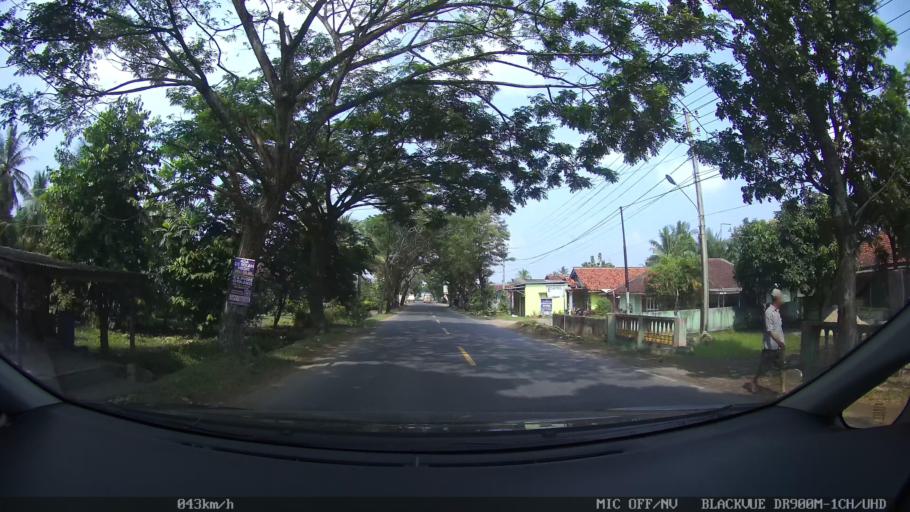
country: ID
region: Lampung
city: Gadingrejo
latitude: -5.3727
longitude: 105.0454
